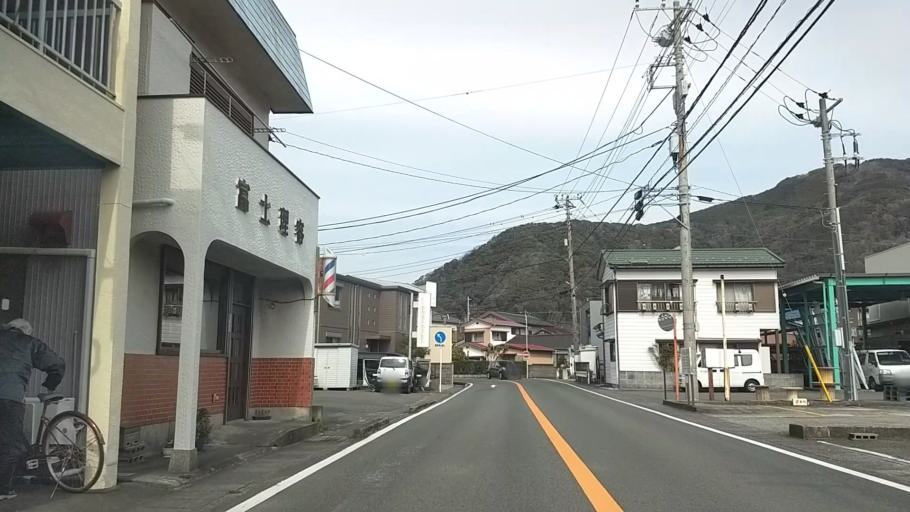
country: JP
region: Shizuoka
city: Shimoda
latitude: 34.6857
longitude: 138.9439
